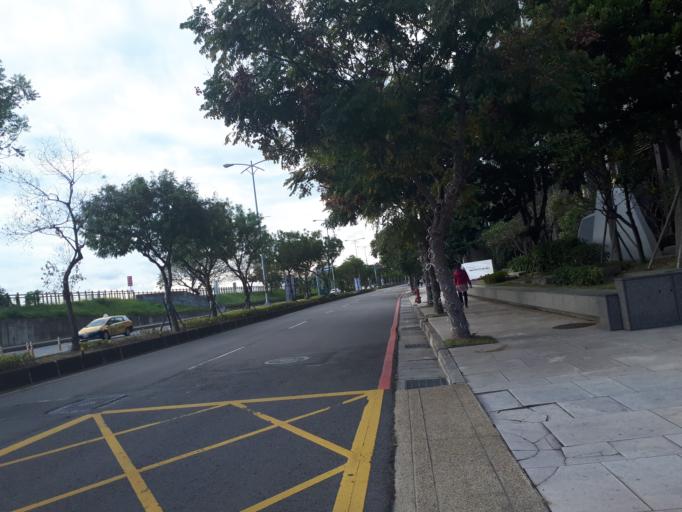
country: TW
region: Taiwan
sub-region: Hsinchu
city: Zhubei
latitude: 24.8005
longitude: 121.0361
